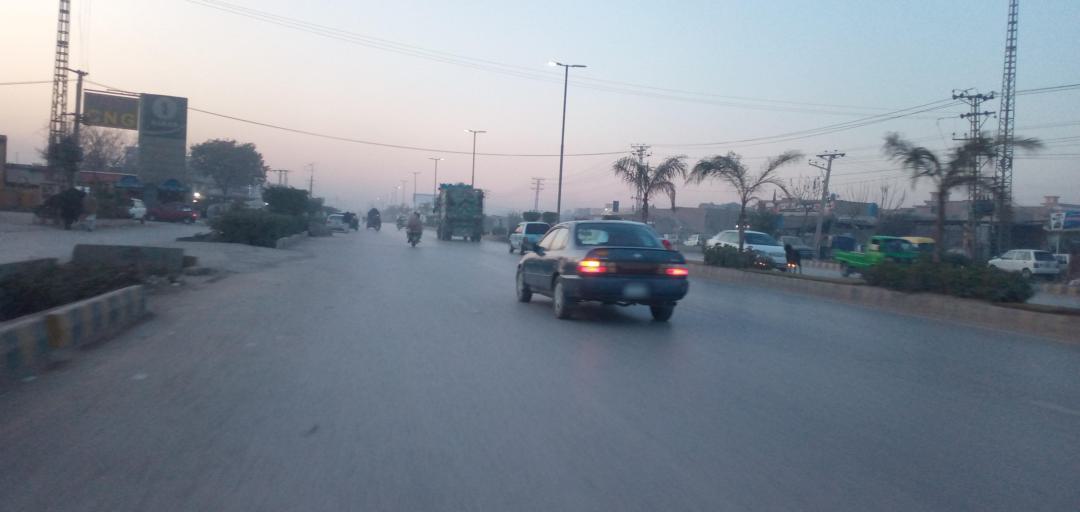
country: PK
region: Khyber Pakhtunkhwa
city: Peshawar
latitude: 34.0300
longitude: 71.6116
